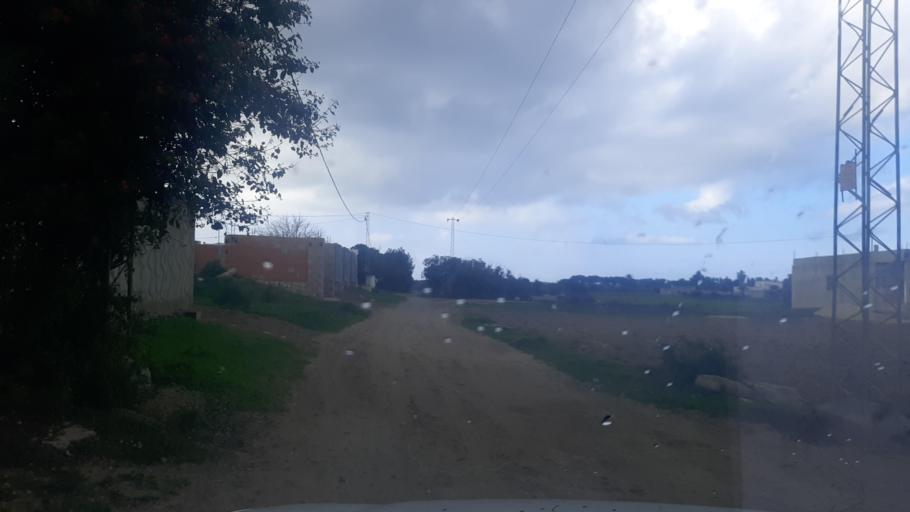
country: TN
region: Nabul
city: Manzil Bu Zalafah
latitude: 36.7379
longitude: 10.5231
